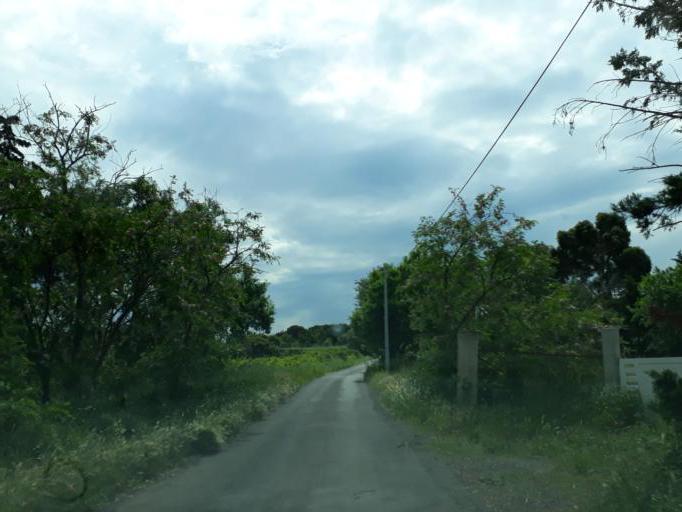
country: FR
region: Languedoc-Roussillon
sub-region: Departement de l'Herault
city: Agde
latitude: 43.2970
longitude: 3.4870
